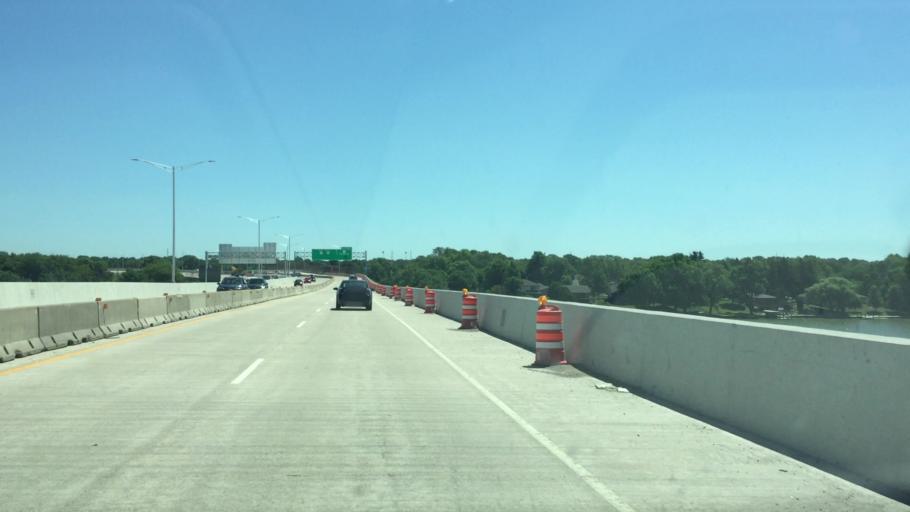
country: US
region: Wisconsin
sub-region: Winnebago County
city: Menasha
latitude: 44.2180
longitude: -88.4590
